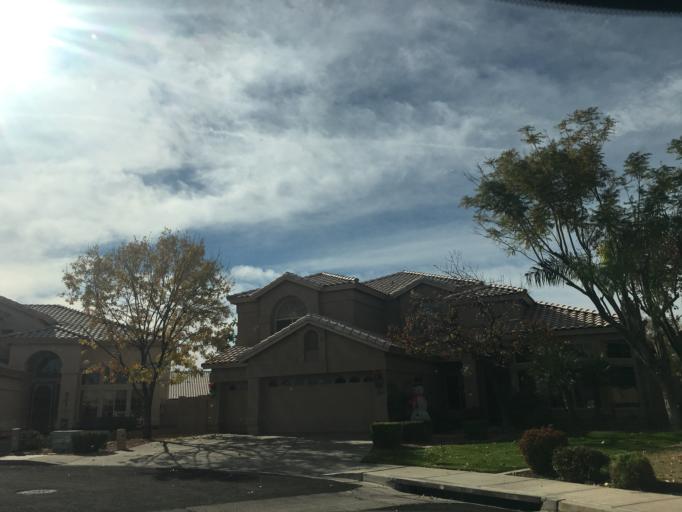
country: US
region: Arizona
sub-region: Maricopa County
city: Gilbert
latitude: 33.3449
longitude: -111.8098
